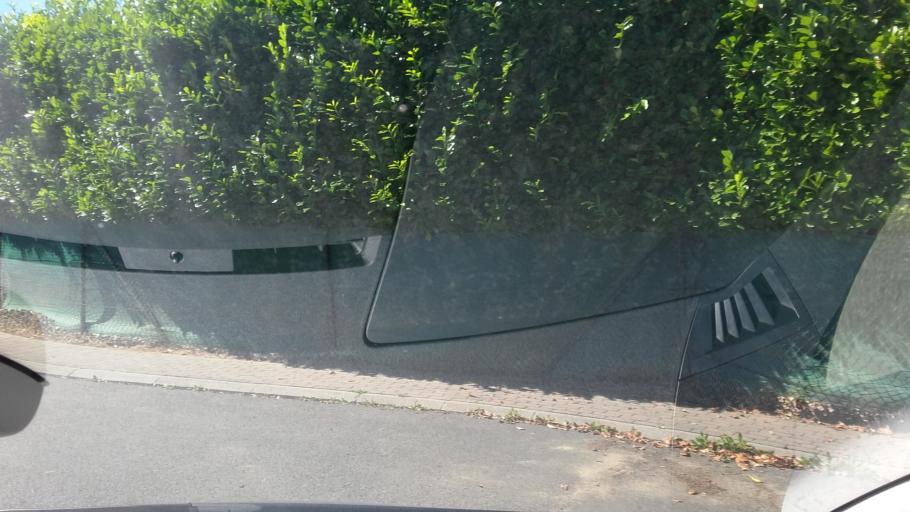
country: BE
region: Wallonia
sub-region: Province du Brabant Wallon
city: Waterloo
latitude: 50.6962
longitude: 4.4155
